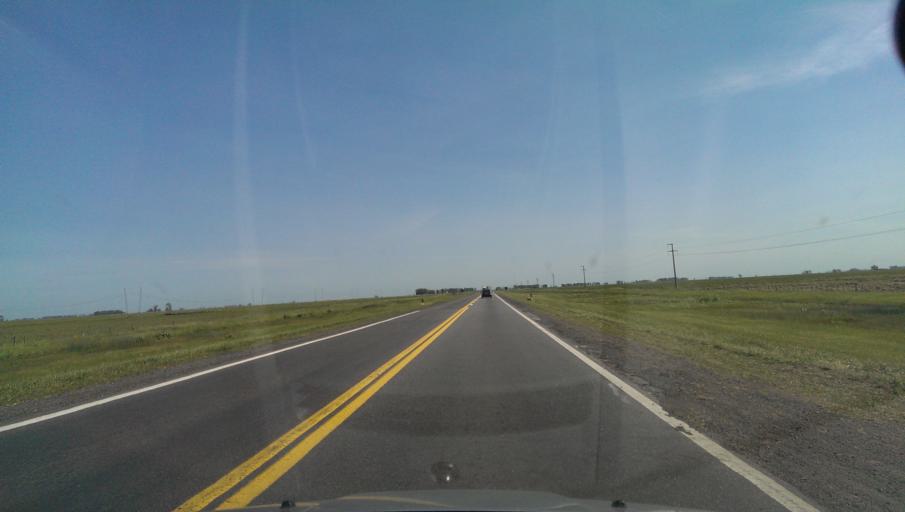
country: AR
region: Buenos Aires
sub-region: Partido de Azul
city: Azul
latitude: -36.5845
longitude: -59.6467
